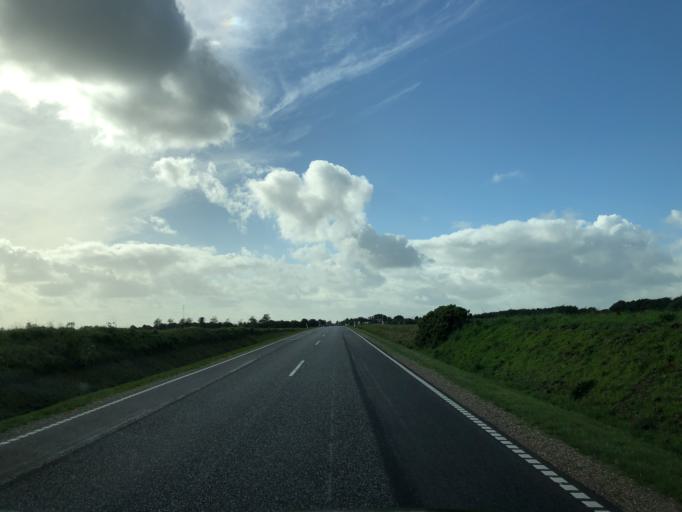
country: DK
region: Central Jutland
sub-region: Holstebro Kommune
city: Ulfborg
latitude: 56.3668
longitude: 8.4425
